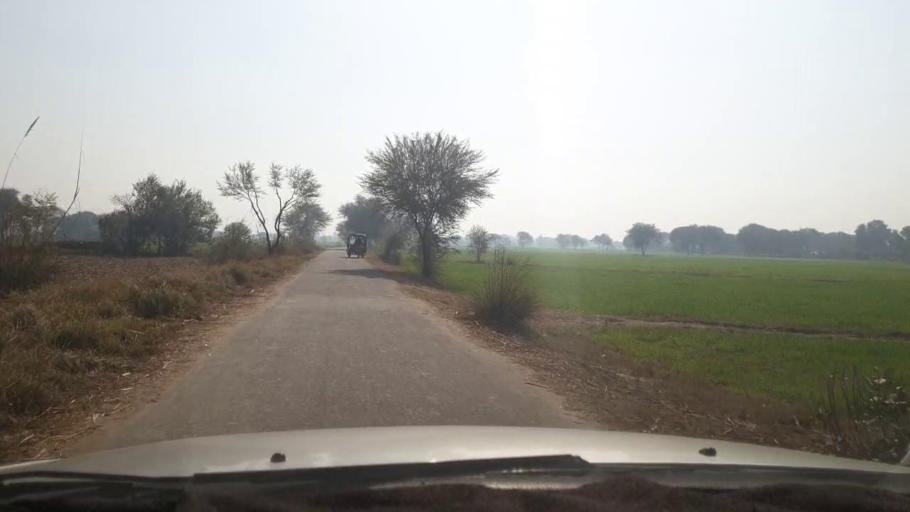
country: PK
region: Sindh
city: Khanpur
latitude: 27.7445
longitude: 69.5039
